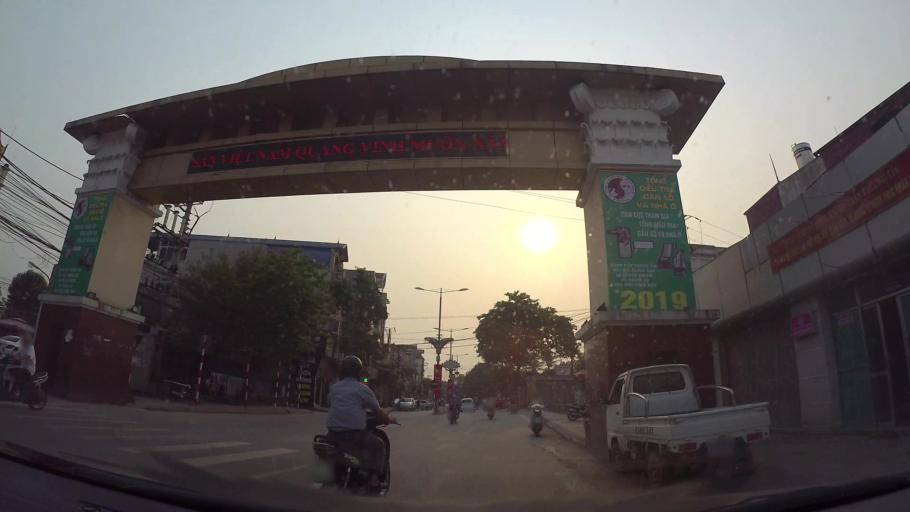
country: VN
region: Ha Noi
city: Thuong Tin
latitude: 20.8696
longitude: 105.8648
